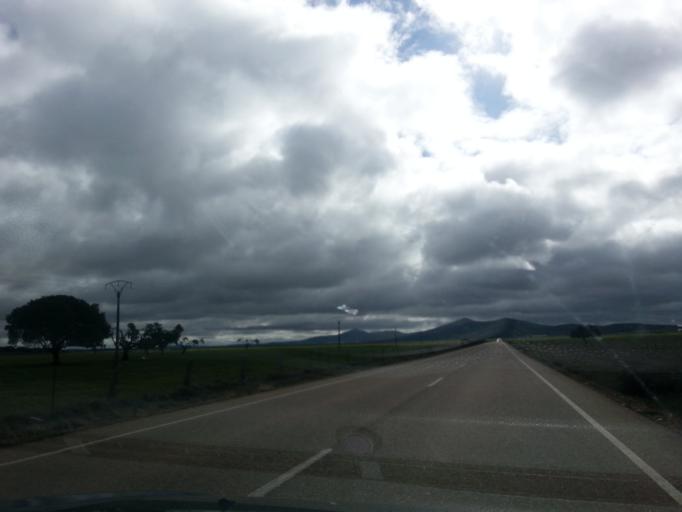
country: ES
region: Castille and Leon
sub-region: Provincia de Salamanca
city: Tamames
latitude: 40.6788
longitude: -6.1275
